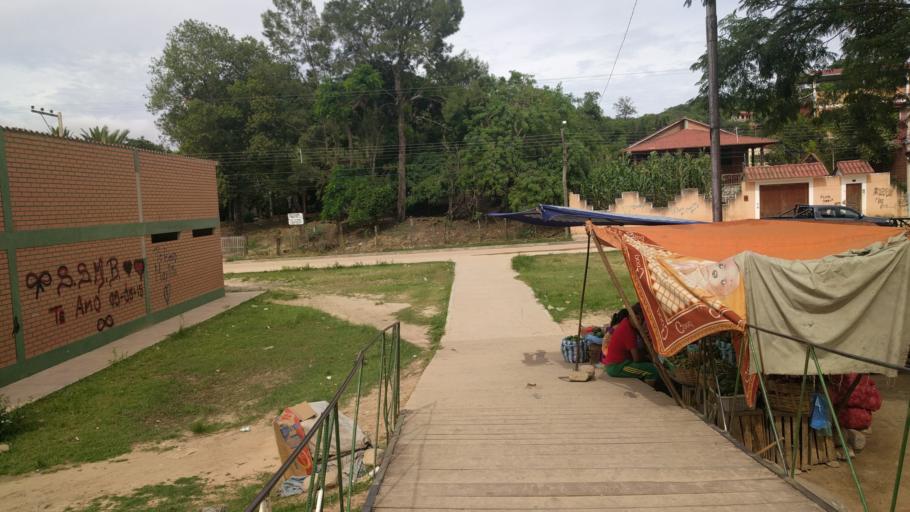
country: BO
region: Chuquisaca
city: Monteagudo
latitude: -19.8031
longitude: -63.9570
